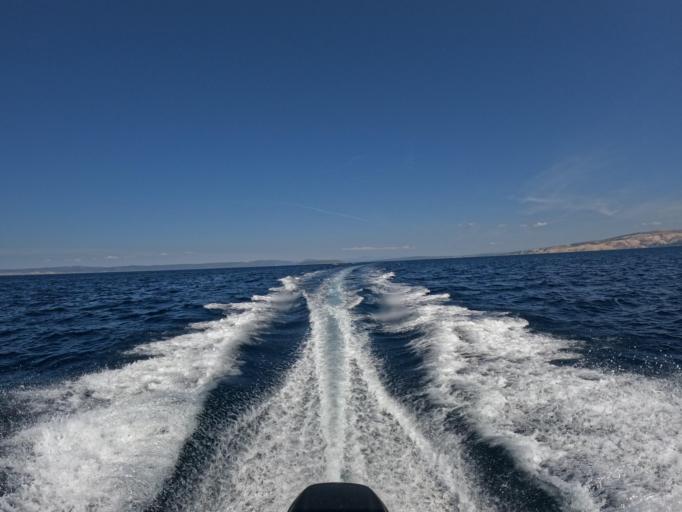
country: HR
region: Primorsko-Goranska
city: Lopar
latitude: 44.8885
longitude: 14.6471
